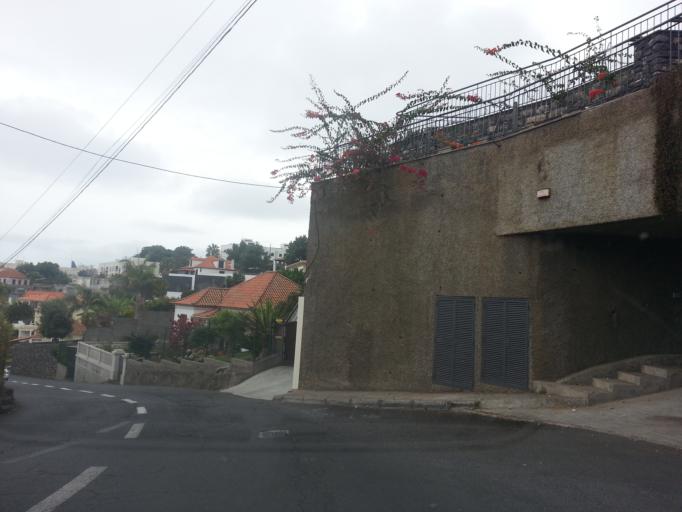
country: PT
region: Madeira
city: Camara de Lobos
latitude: 32.6484
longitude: -16.9343
